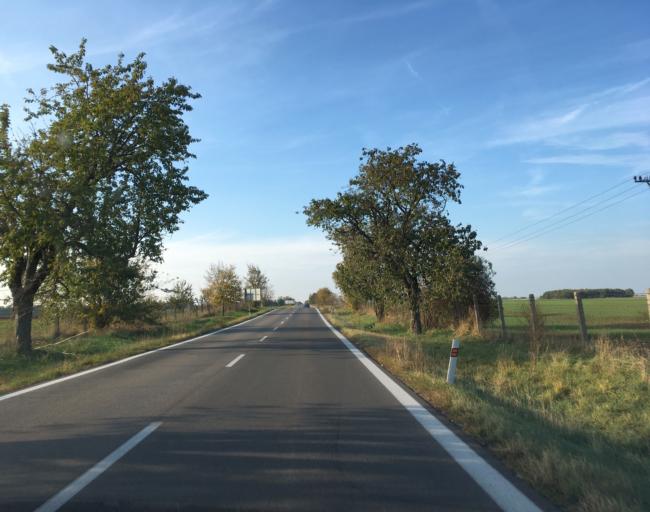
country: SK
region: Nitriansky
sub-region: Okres Nove Zamky
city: Nove Zamky
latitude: 48.0198
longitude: 18.1459
